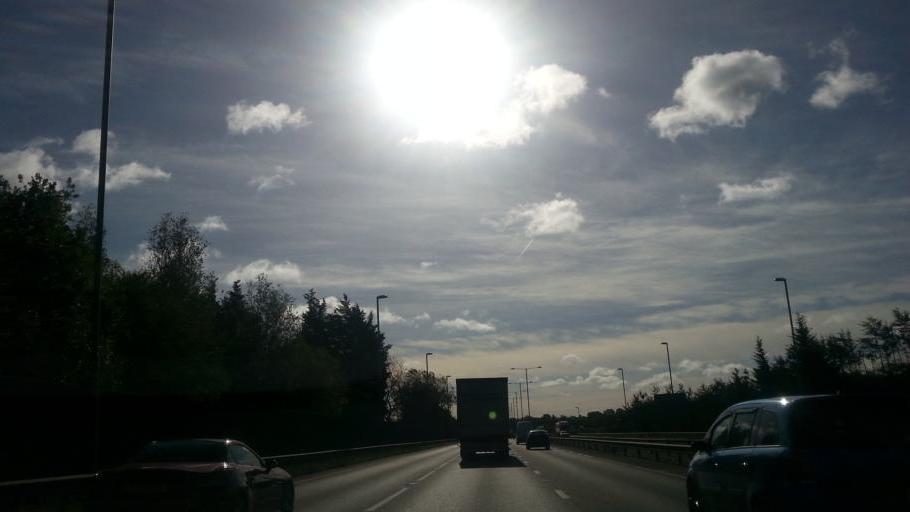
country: GB
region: England
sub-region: Northamptonshire
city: Kettering
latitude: 52.3828
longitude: -0.7312
